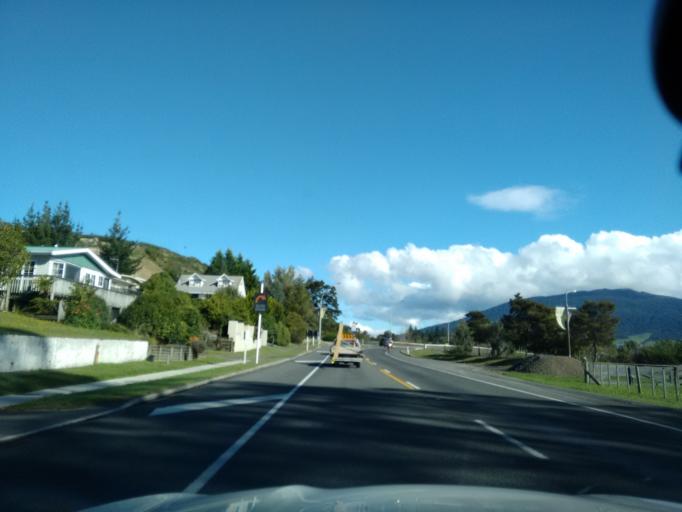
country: NZ
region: Waikato
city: Turangi
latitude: -38.9845
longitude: 175.8199
